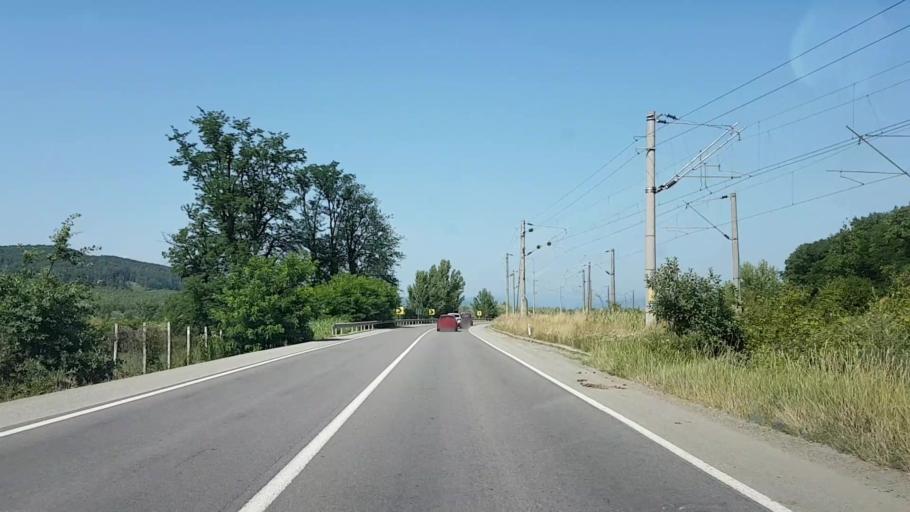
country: RO
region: Bistrita-Nasaud
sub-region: Comuna Beclean
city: Beclean
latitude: 47.1844
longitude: 24.1928
